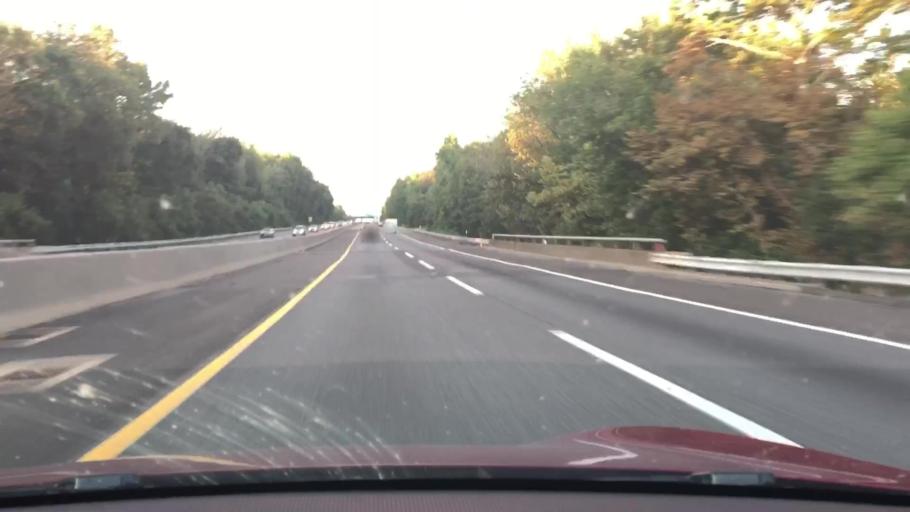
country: US
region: New Jersey
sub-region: Gloucester County
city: Swedesboro
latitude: 39.7465
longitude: -75.2876
